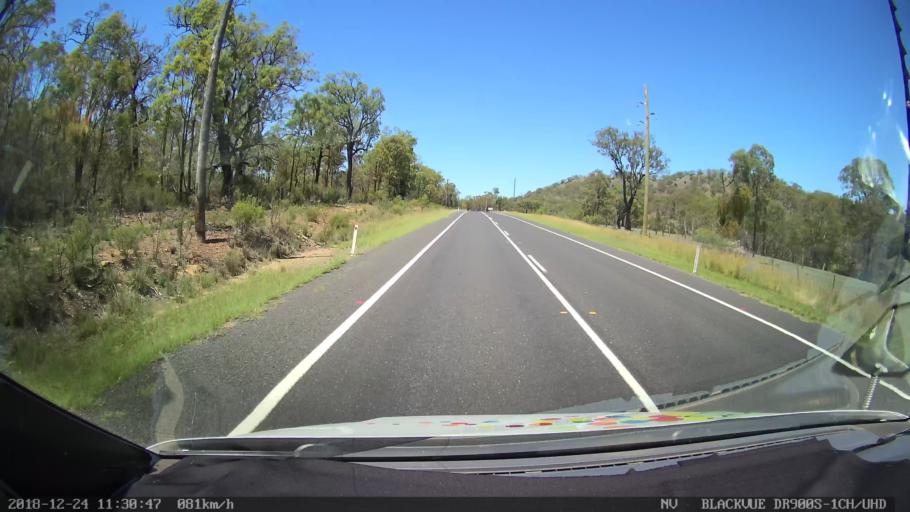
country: AU
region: New South Wales
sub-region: Upper Hunter Shire
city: Merriwa
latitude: -32.2083
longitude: 150.4637
